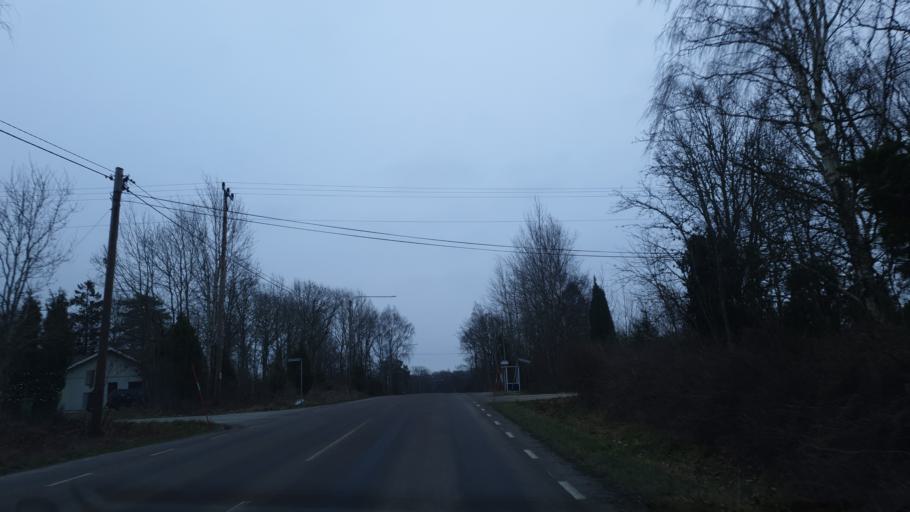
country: SE
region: Blekinge
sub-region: Karlskrona Kommun
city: Sturko
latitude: 56.1124
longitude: 15.7016
